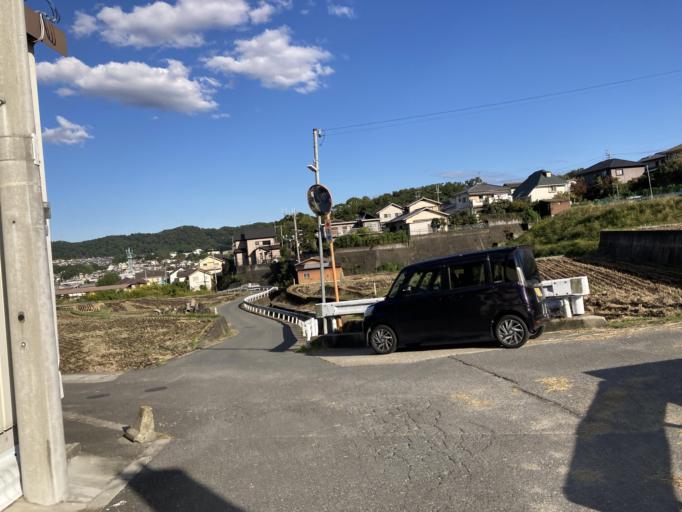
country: JP
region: Nara
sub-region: Ikoma-shi
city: Ikoma
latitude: 34.6696
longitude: 135.6995
